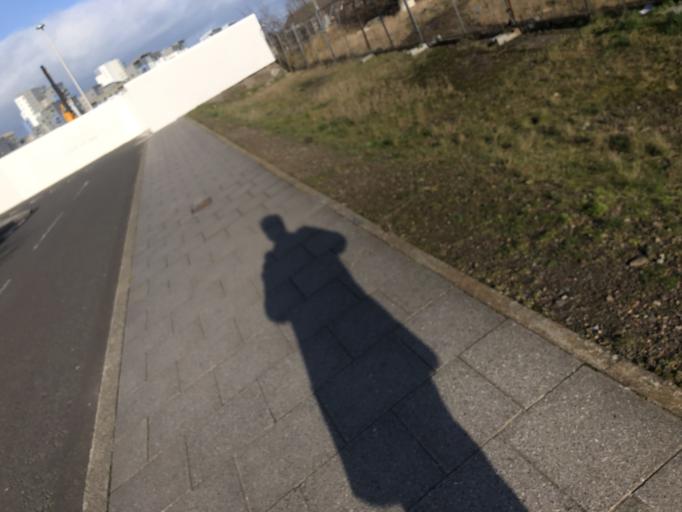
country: GB
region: Scotland
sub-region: Edinburgh
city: Edinburgh
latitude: 55.9827
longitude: -3.1922
